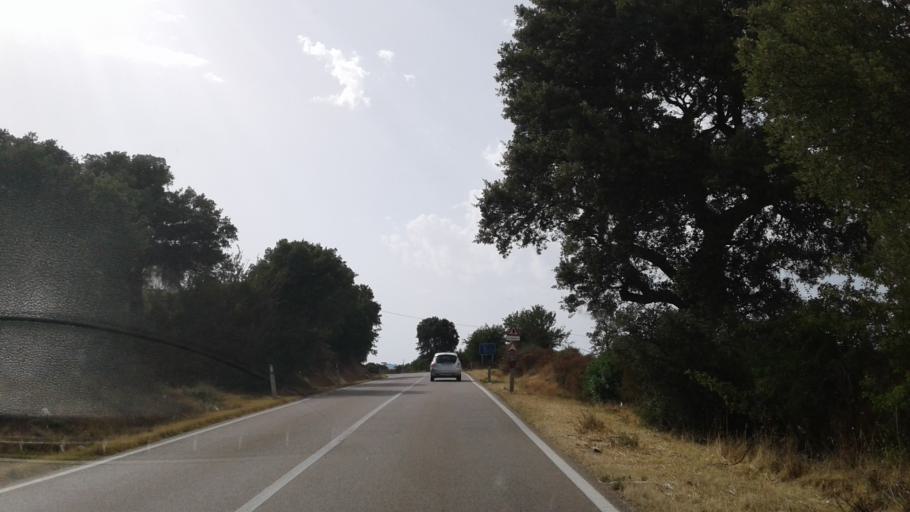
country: IT
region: Sardinia
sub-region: Provincia di Olbia-Tempio
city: Sant'Antonio di Gallura
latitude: 40.9632
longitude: 9.2837
